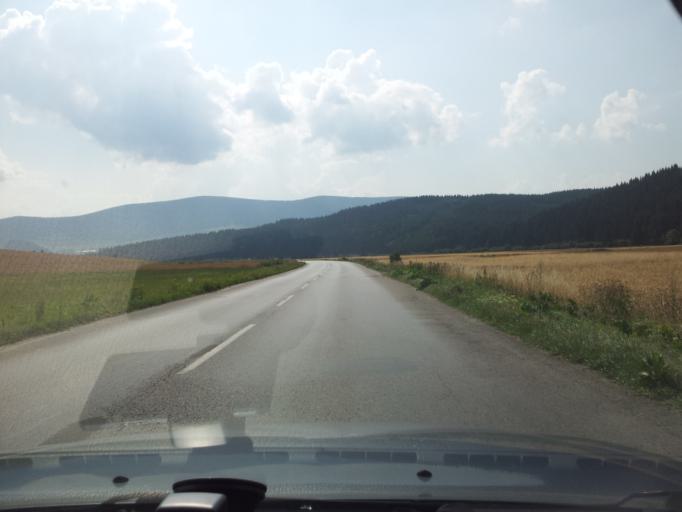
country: SK
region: Zilinsky
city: Namestovo
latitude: 49.3762
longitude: 19.3887
